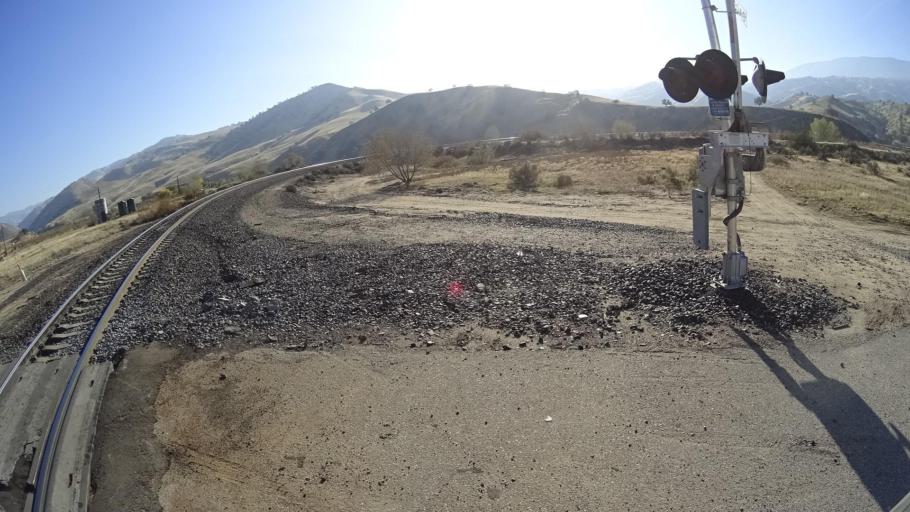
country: US
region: California
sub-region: Kern County
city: Bear Valley Springs
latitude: 35.2921
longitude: -118.6250
